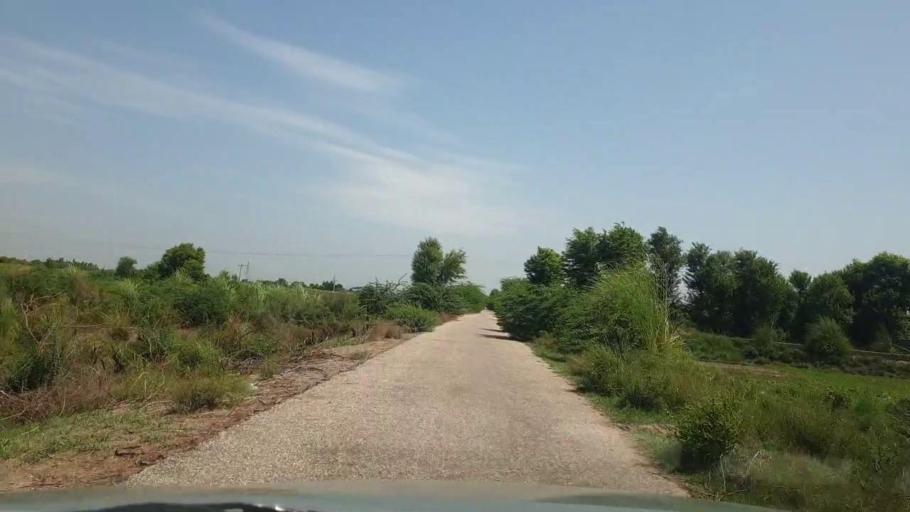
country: PK
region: Sindh
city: Bozdar
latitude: 27.0902
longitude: 68.9678
